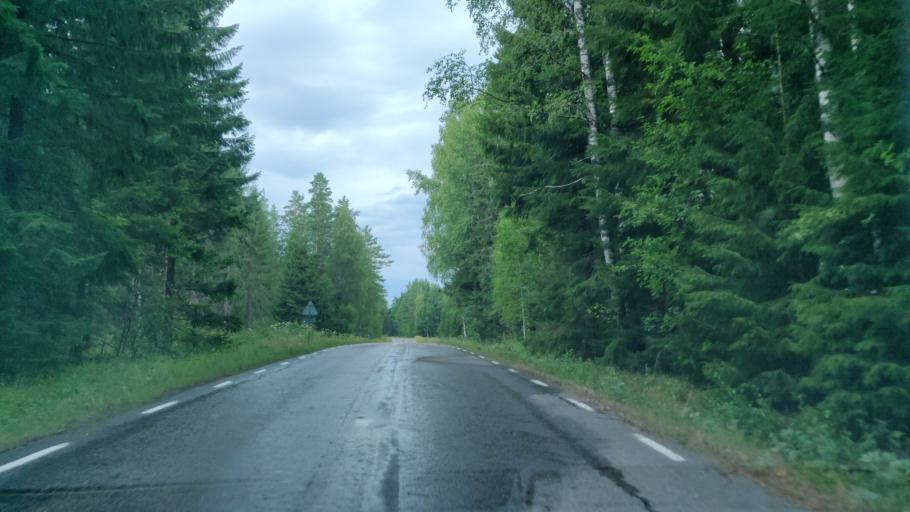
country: SE
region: Vaermland
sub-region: Munkfors Kommun
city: Munkfors
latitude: 59.8772
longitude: 13.5225
